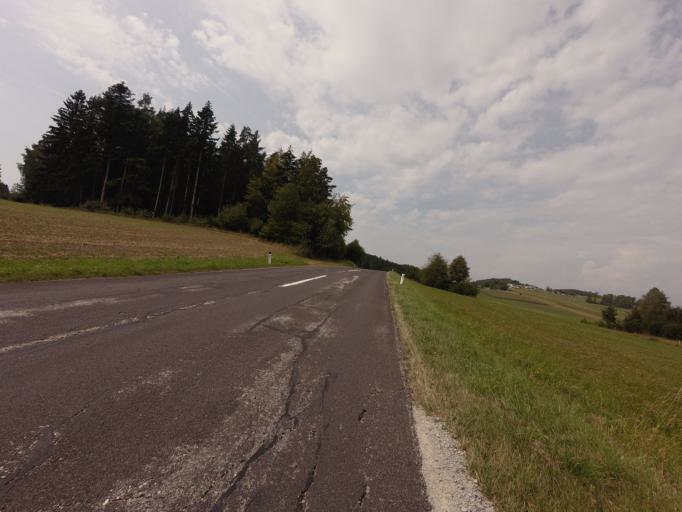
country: AT
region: Upper Austria
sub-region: Politischer Bezirk Urfahr-Umgebung
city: Reichenthal
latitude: 48.5523
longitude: 14.4233
